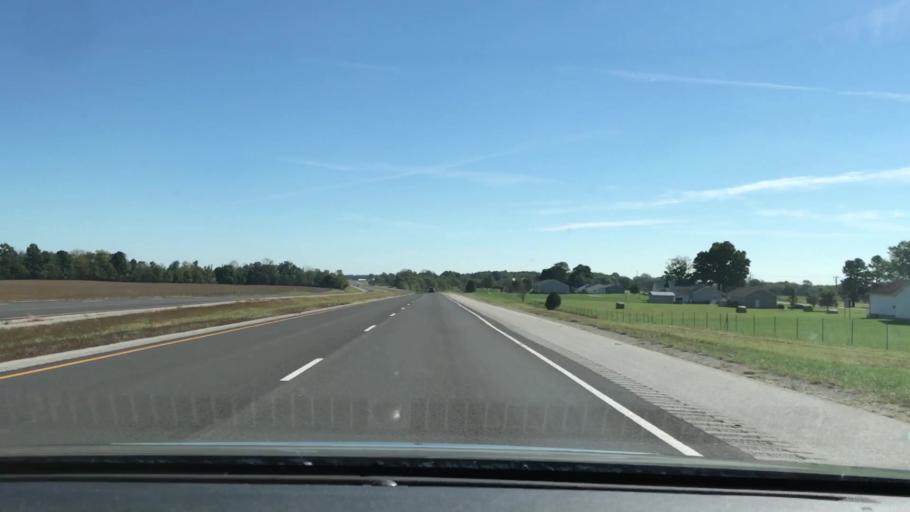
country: US
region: Kentucky
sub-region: Todd County
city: Elkton
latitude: 36.8028
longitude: -87.0936
